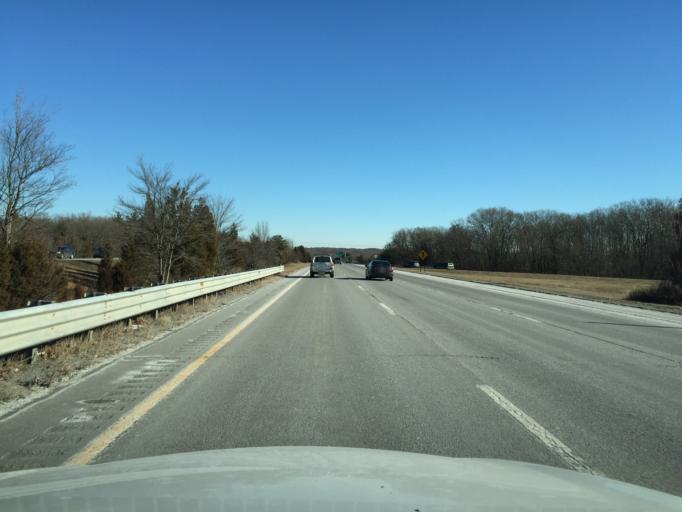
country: US
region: Massachusetts
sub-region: Norfolk County
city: Wrentham
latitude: 42.0375
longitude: -71.3112
